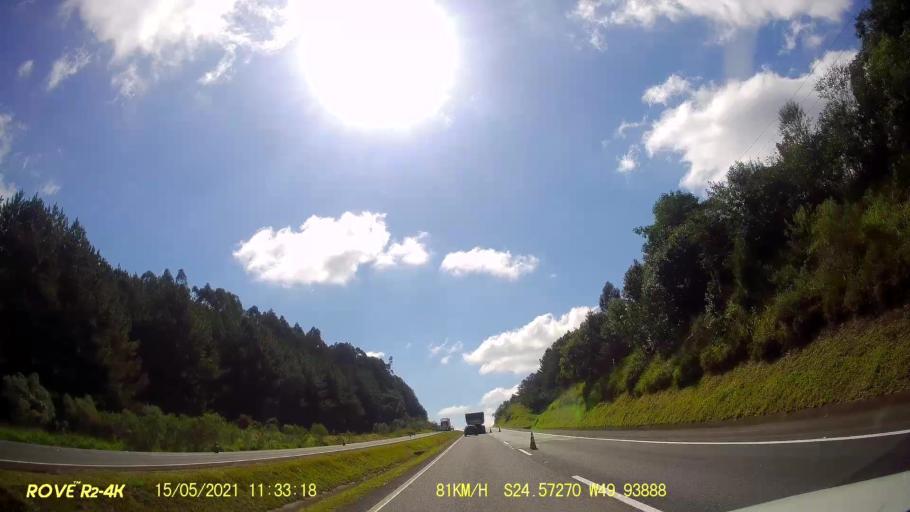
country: BR
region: Parana
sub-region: Pirai Do Sul
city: Pirai do Sul
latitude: -24.5726
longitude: -49.9388
